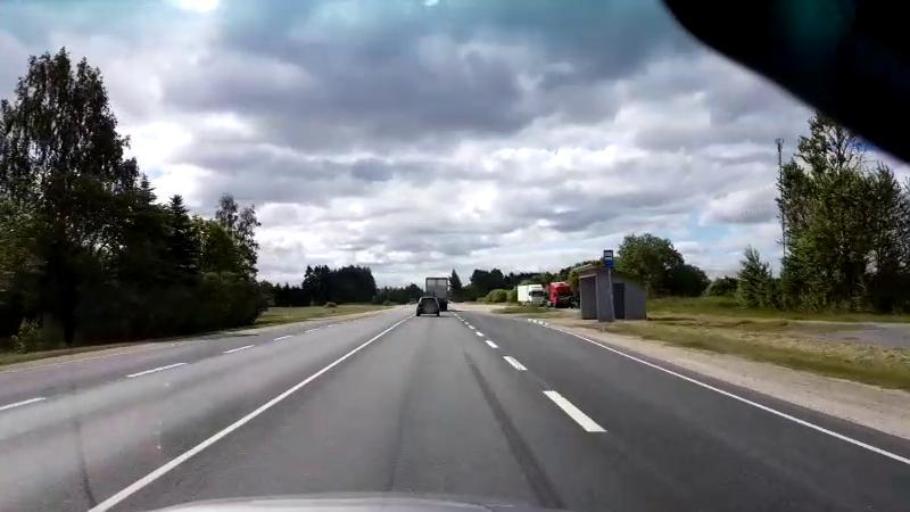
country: EE
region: Raplamaa
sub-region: Maerjamaa vald
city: Marjamaa
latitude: 58.7691
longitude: 24.4172
